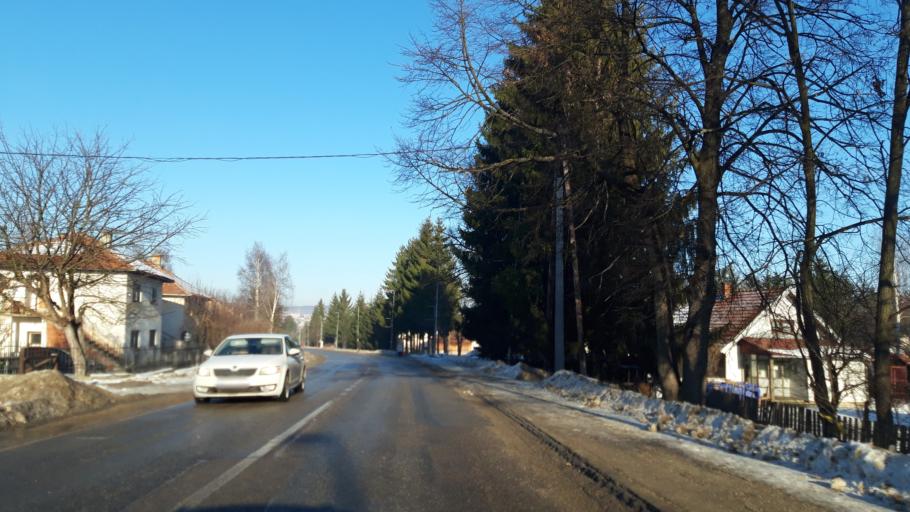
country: BA
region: Republika Srpska
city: Sokolac
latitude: 43.9288
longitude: 18.7873
